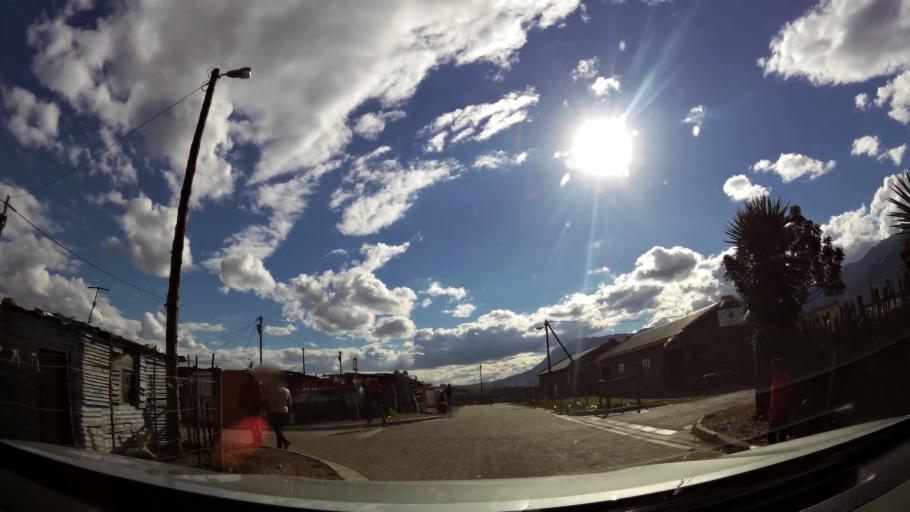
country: ZA
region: Western Cape
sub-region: Overberg District Municipality
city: Swellendam
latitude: -34.0455
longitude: 20.4392
